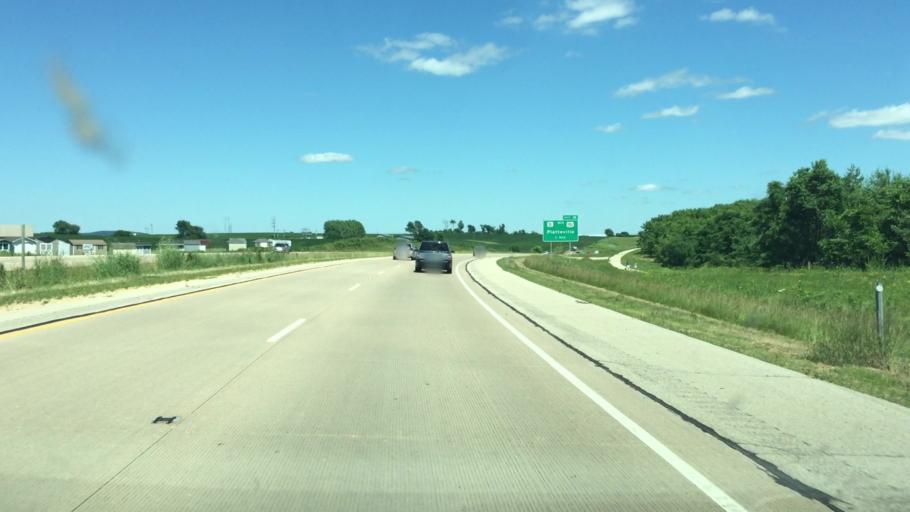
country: US
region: Wisconsin
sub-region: Grant County
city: Platteville
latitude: 42.7105
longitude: -90.5129
